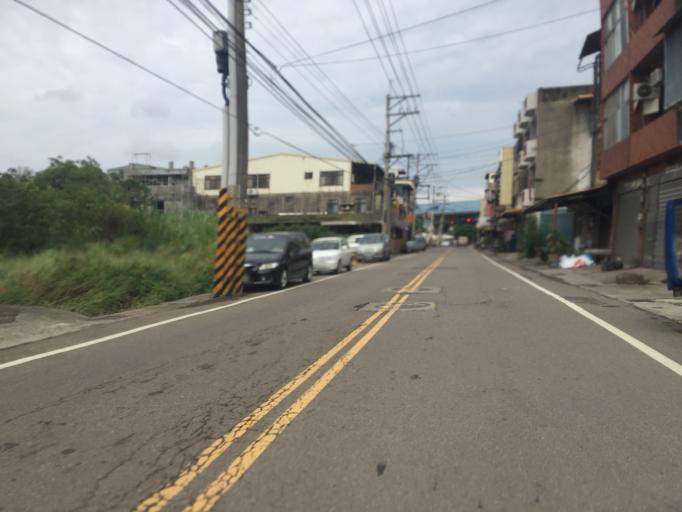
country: TW
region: Taiwan
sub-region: Hsinchu
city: Hsinchu
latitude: 24.7082
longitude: 120.8874
